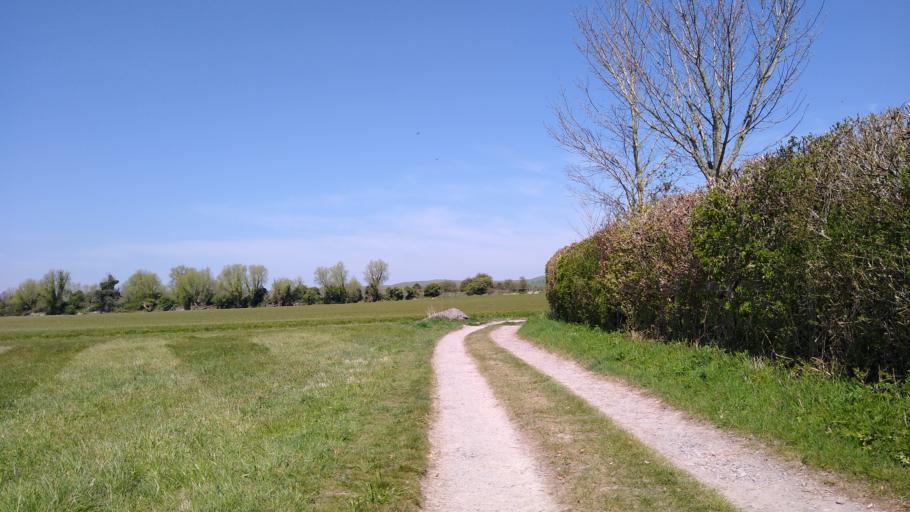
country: GB
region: England
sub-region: Wiltshire
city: Avebury
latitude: 51.3594
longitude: -1.8995
